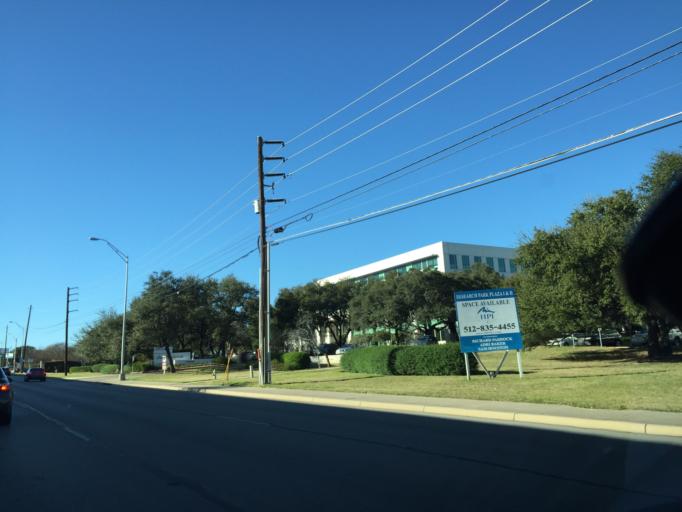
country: US
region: Texas
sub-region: Williamson County
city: Jollyville
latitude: 30.4285
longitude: -97.7571
